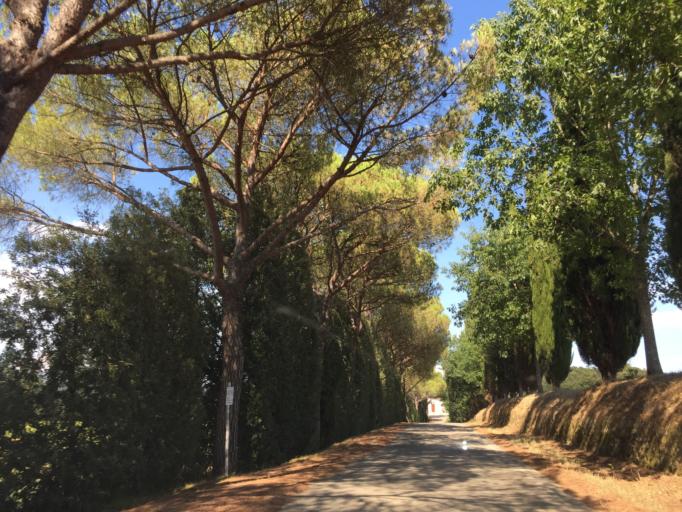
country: IT
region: Tuscany
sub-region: Provincia di Pistoia
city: Uggia-Pazzera-Bizzarrino
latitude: 43.8223
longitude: 10.8343
